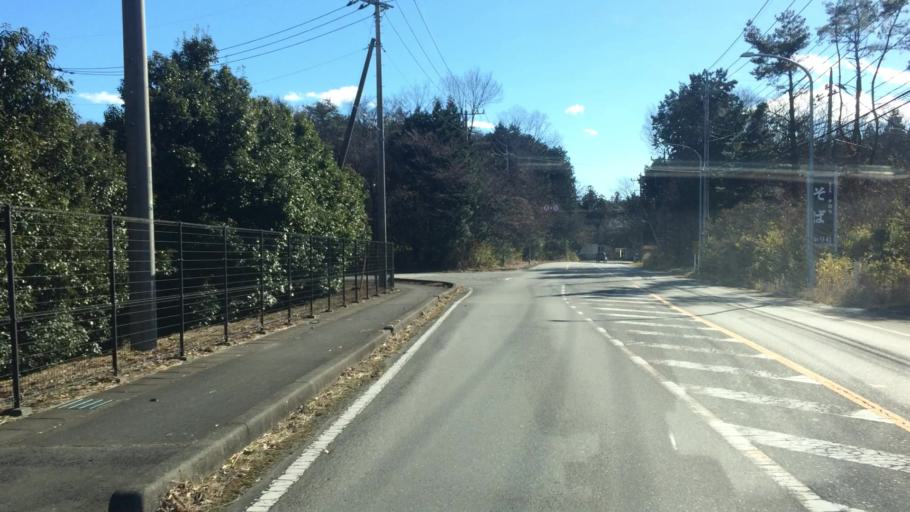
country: JP
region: Tochigi
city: Imaichi
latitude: 36.7562
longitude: 139.7310
